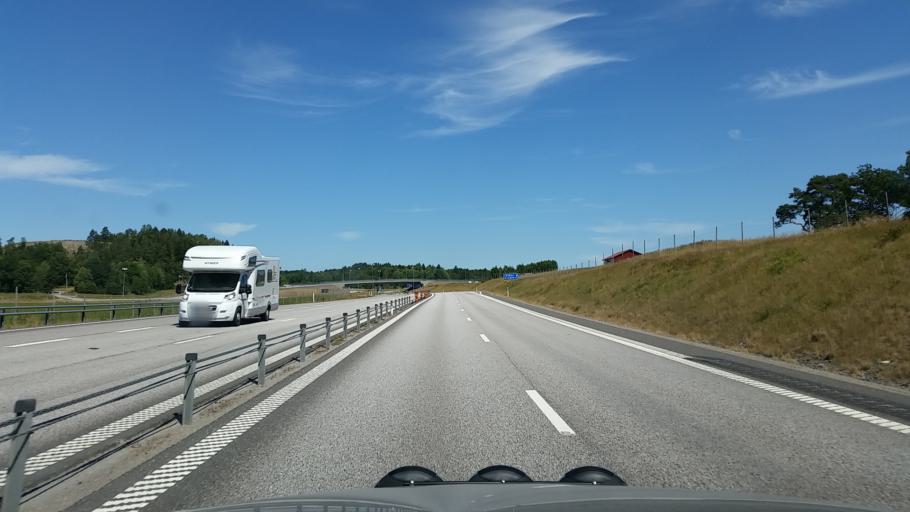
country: SE
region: Vaestra Goetaland
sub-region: Lilla Edets Kommun
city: Lodose
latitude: 58.0347
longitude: 12.1769
